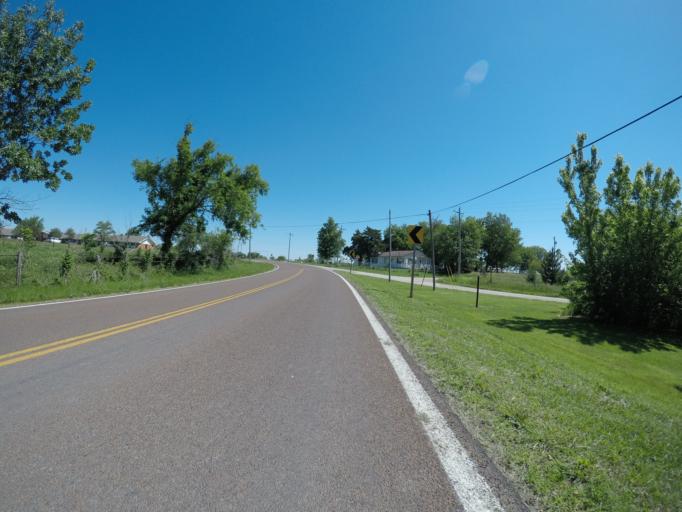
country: US
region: Kansas
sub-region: Wabaunsee County
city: Alma
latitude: 38.8634
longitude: -96.1045
